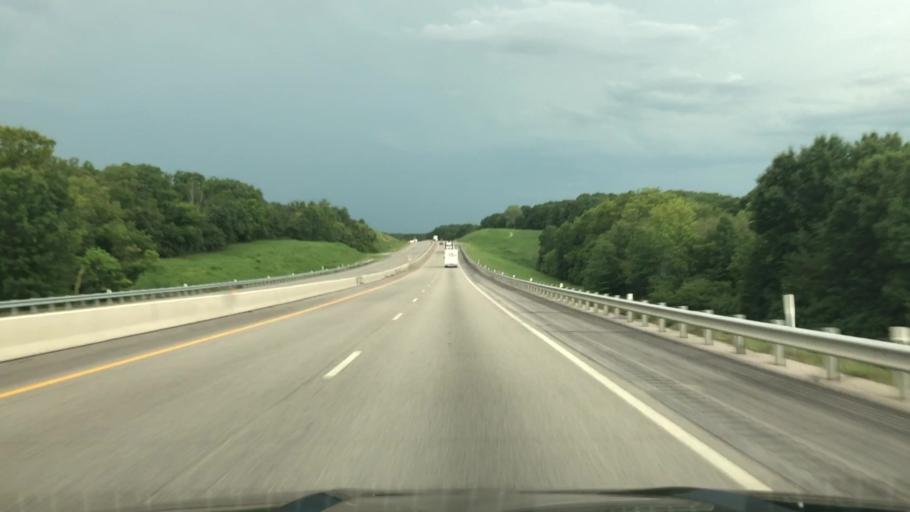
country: US
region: Oklahoma
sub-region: Rogers County
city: Justice
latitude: 36.3397
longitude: -95.5005
